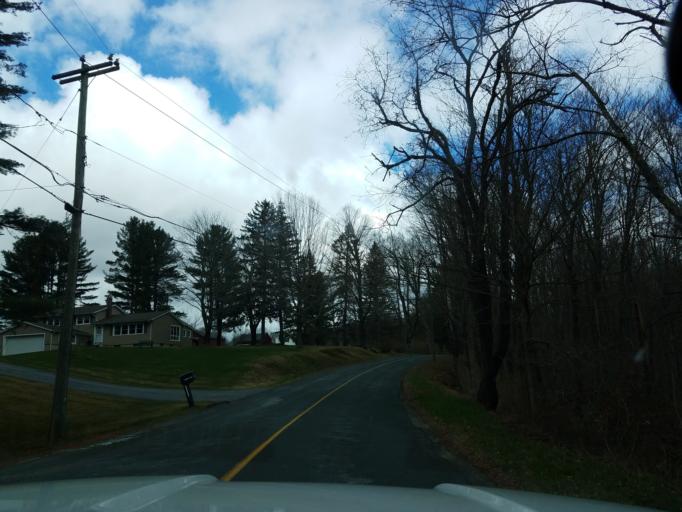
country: US
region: Connecticut
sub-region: Litchfield County
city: Litchfield
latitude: 41.7704
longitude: -73.1762
